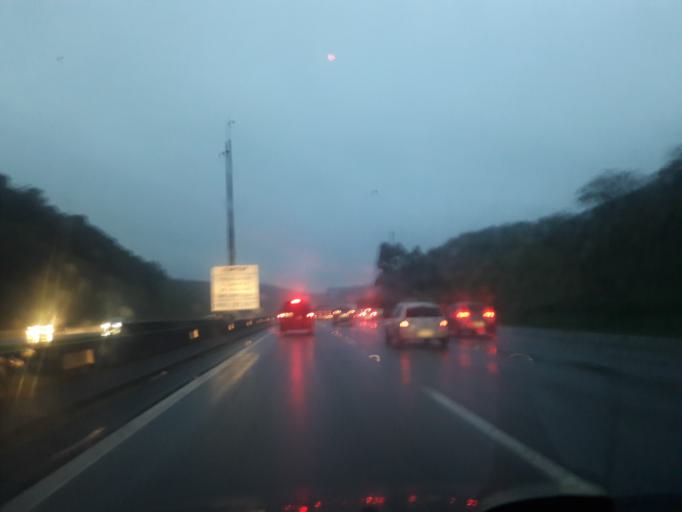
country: BR
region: Sao Paulo
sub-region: Sao Bernardo Do Campo
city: Sao Bernardo do Campo
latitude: -23.7608
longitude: -46.5731
